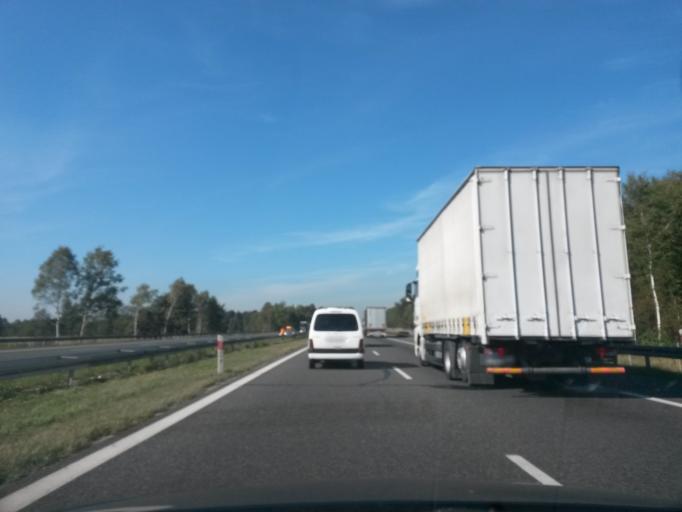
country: PL
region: Lesser Poland Voivodeship
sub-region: Powiat chrzanowski
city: Bolecin
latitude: 50.1119
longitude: 19.5084
